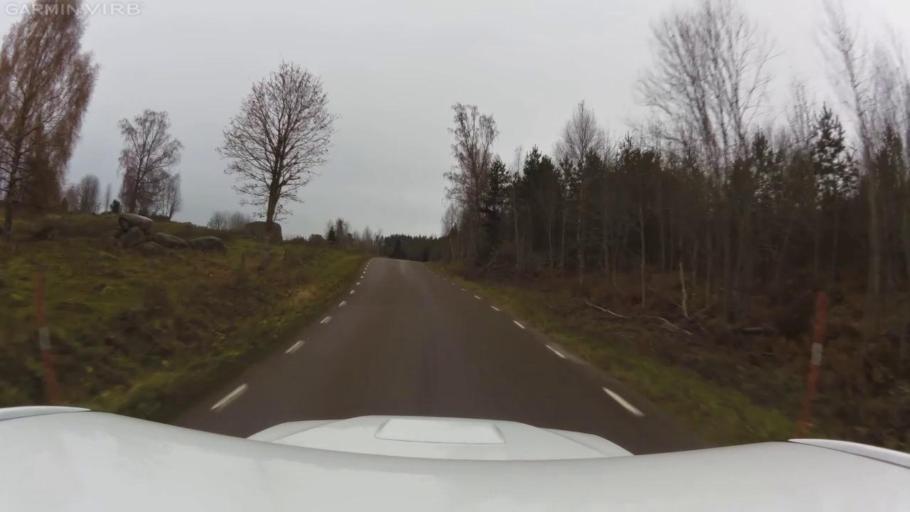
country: SE
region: OEstergoetland
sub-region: Mjolby Kommun
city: Mantorp
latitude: 58.1551
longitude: 15.3898
